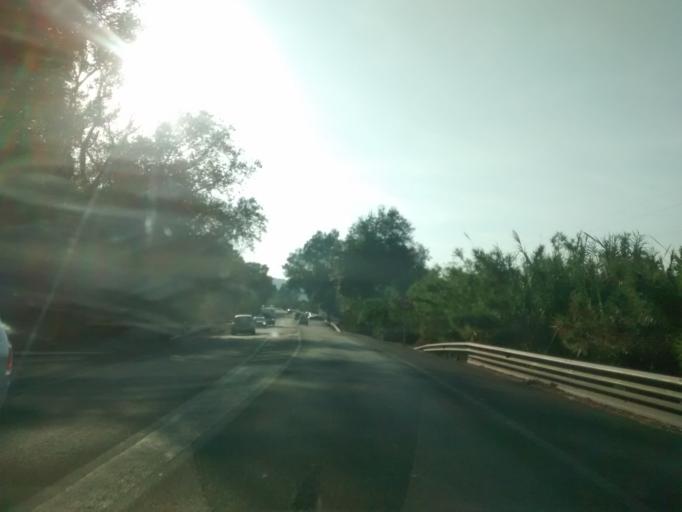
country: ES
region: Andalusia
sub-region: Provincia de Cadiz
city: Vejer de la Frontera
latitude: 36.2608
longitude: -5.9628
